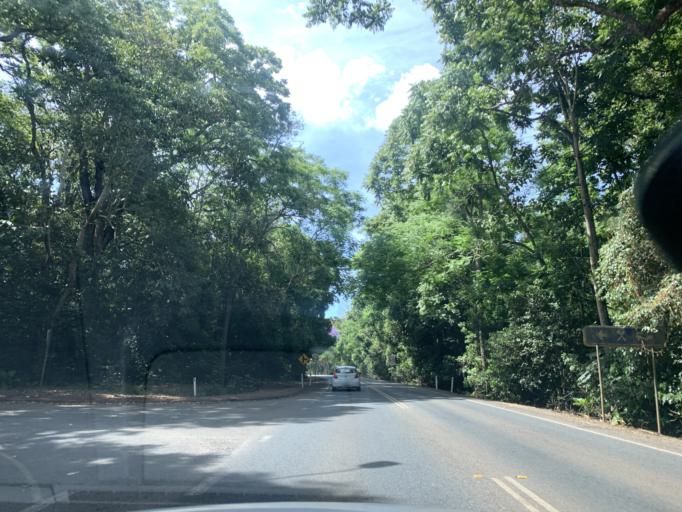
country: AU
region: Queensland
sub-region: Tablelands
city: Tolga
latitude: -17.2340
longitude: 145.4794
